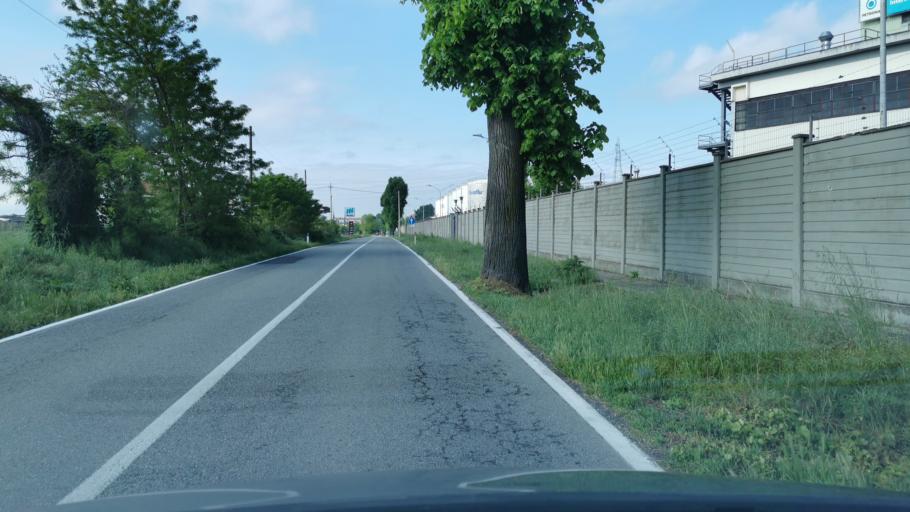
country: IT
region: Piedmont
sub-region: Provincia di Torino
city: Villastellone
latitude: 44.9318
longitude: 7.7560
